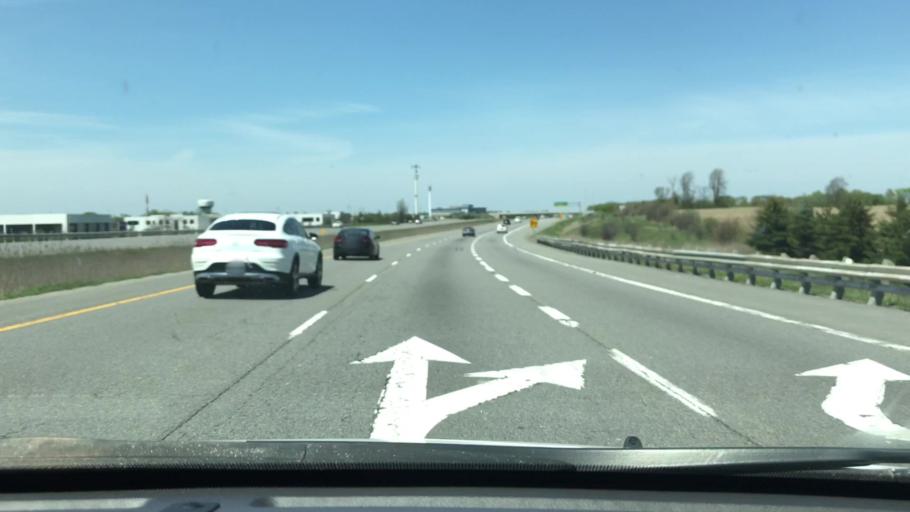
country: CA
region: Ontario
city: Newmarket
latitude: 44.0063
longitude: -79.4046
